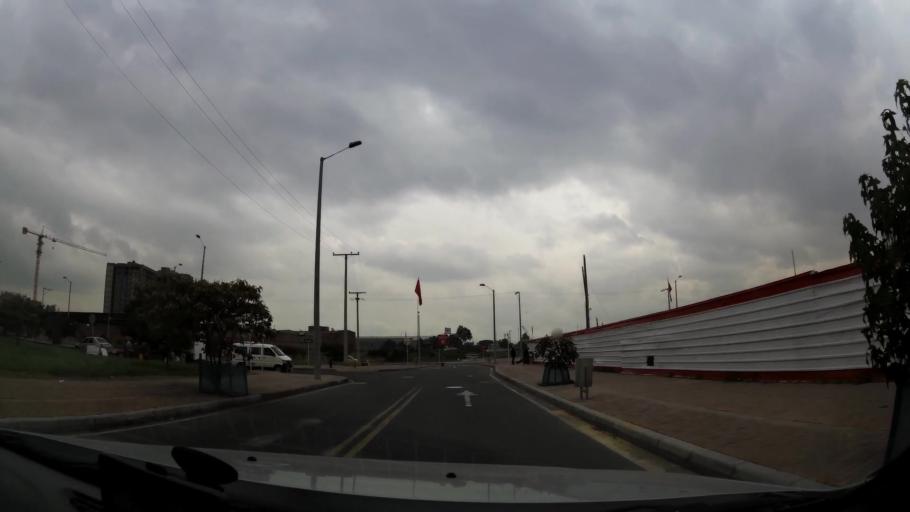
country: CO
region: Bogota D.C.
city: Bogota
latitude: 4.6623
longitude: -74.1122
